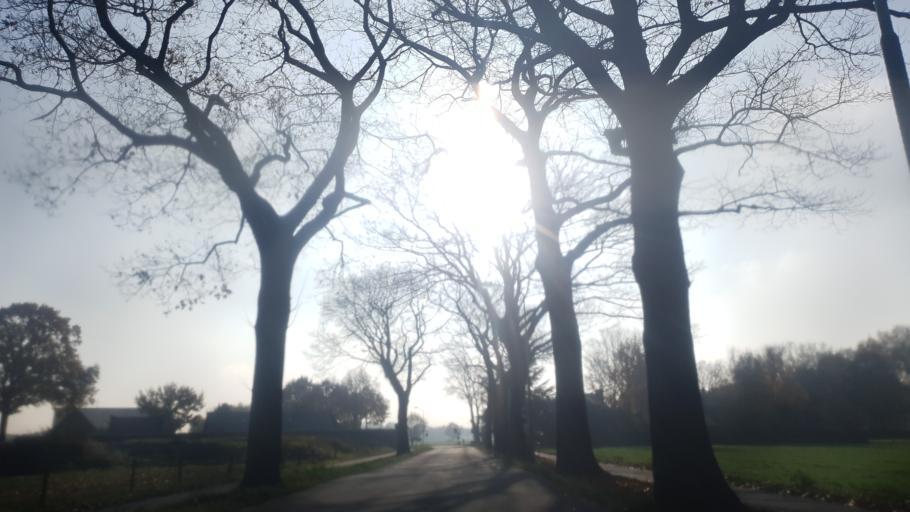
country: NL
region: North Brabant
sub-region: Gemeente Landerd
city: Zeeland
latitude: 51.7201
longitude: 5.6834
